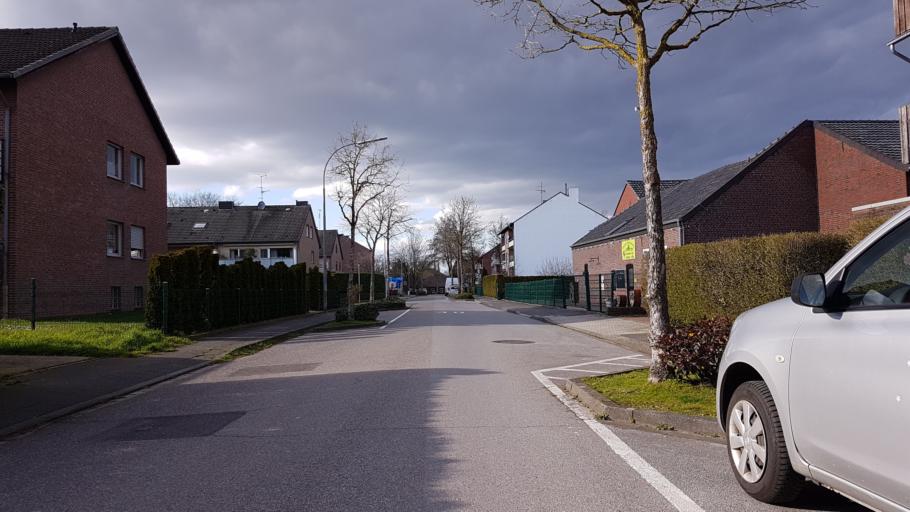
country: DE
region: North Rhine-Westphalia
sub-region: Regierungsbezirk Dusseldorf
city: Schwalmtal
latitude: 51.2266
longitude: 6.2455
